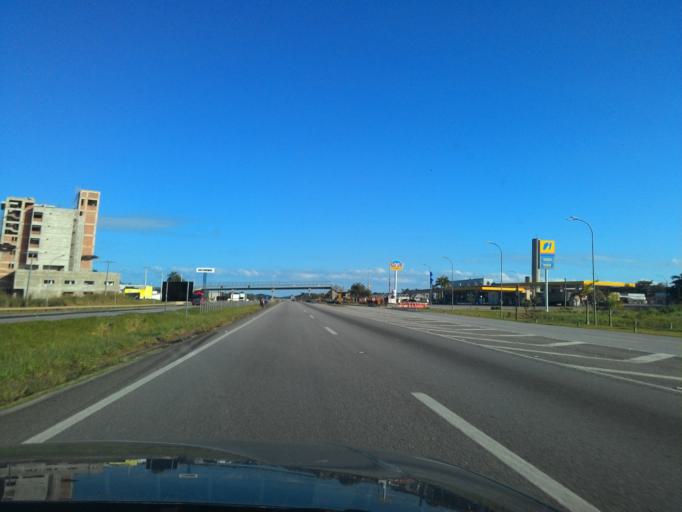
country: BR
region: Sao Paulo
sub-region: Registro
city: Registro
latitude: -24.5278
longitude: -47.8559
